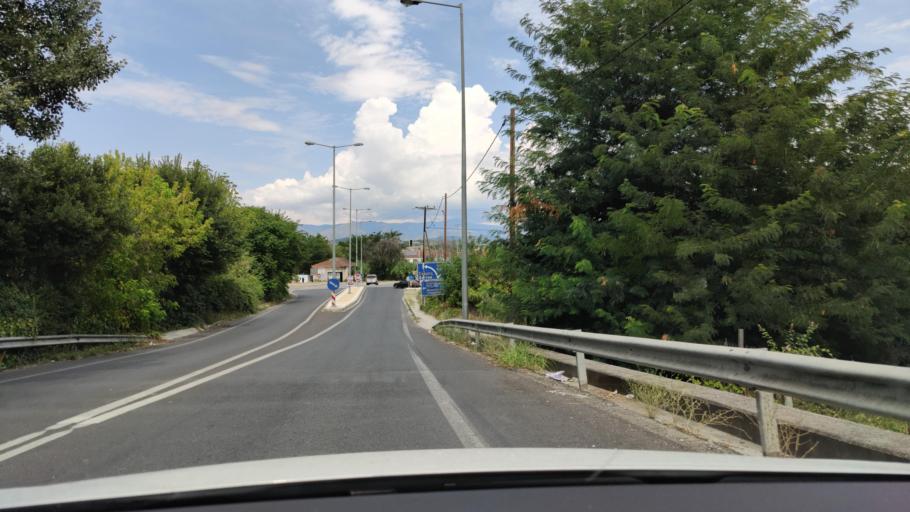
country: GR
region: Central Macedonia
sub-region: Nomos Serron
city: Serres
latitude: 41.0747
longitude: 23.5405
